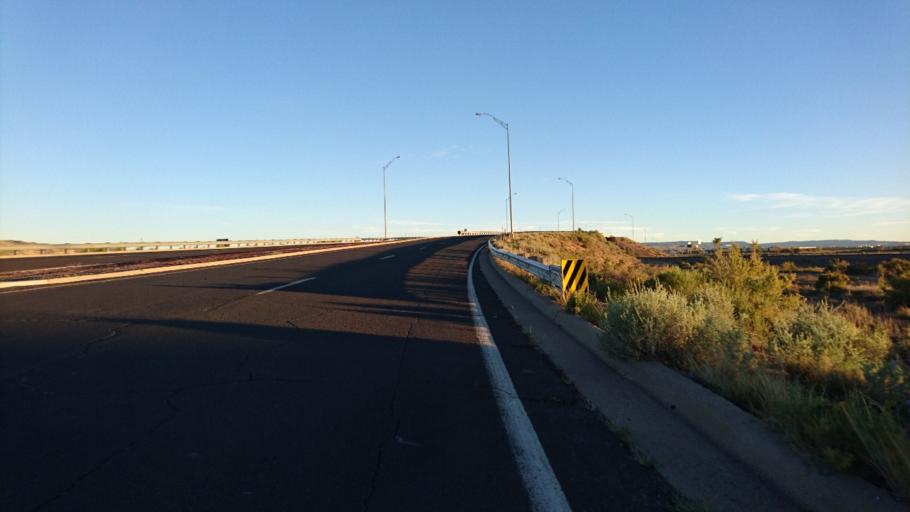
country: US
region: New Mexico
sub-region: Cibola County
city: Grants
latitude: 35.1393
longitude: -107.8288
